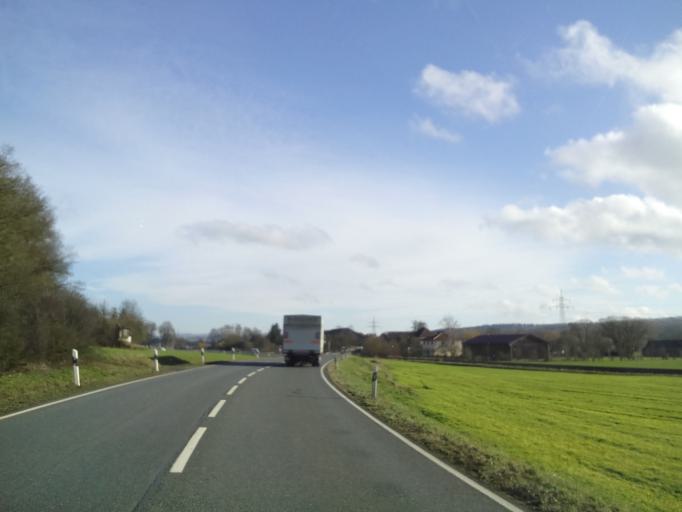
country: DE
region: Bavaria
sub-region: Upper Franconia
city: Altenkunstadt
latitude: 50.1265
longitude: 11.2907
